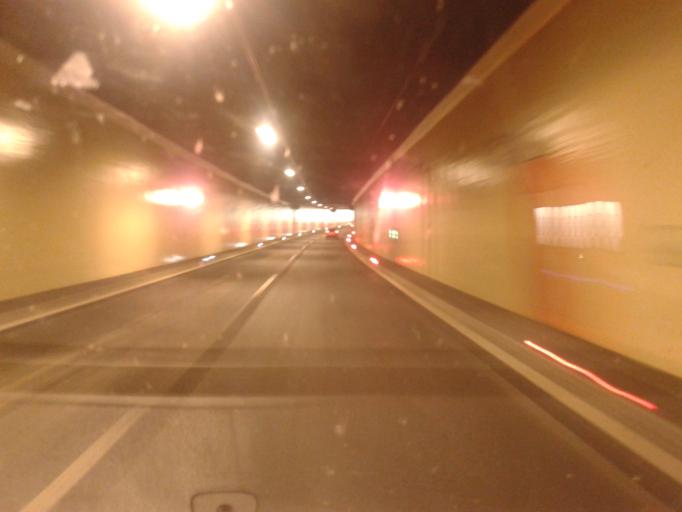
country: AT
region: Carinthia
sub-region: Klagenfurt am Woerthersee
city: Klagenfurt am Woerthersee
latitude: 46.6569
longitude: 14.2799
